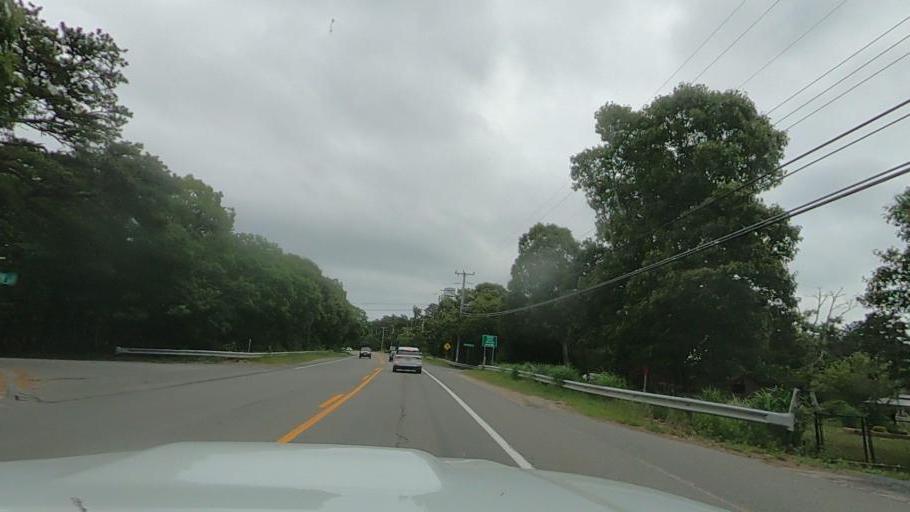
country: US
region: Massachusetts
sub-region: Barnstable County
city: Wellfleet
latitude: 41.9211
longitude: -70.0080
